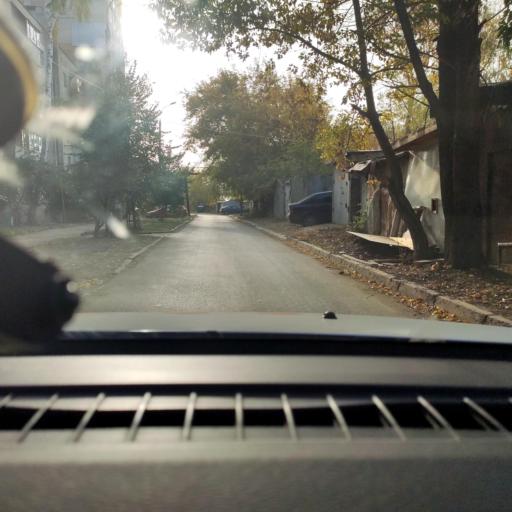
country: RU
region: Samara
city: Samara
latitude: 53.1209
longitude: 50.0783
